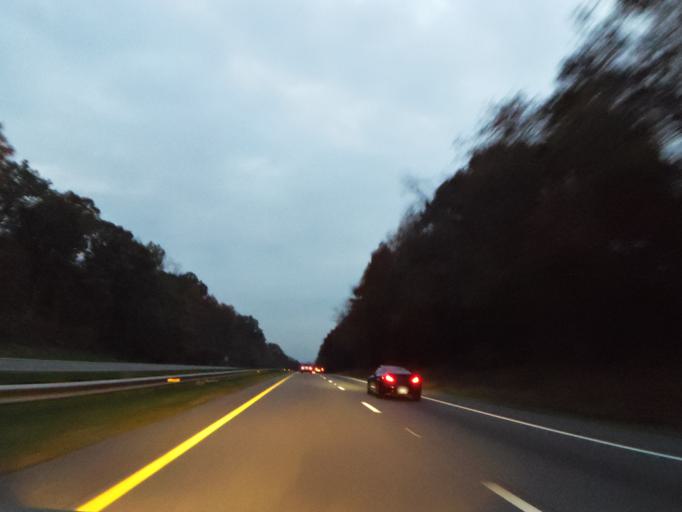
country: US
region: North Carolina
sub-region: McDowell County
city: West Marion
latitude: 35.6358
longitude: -82.0980
